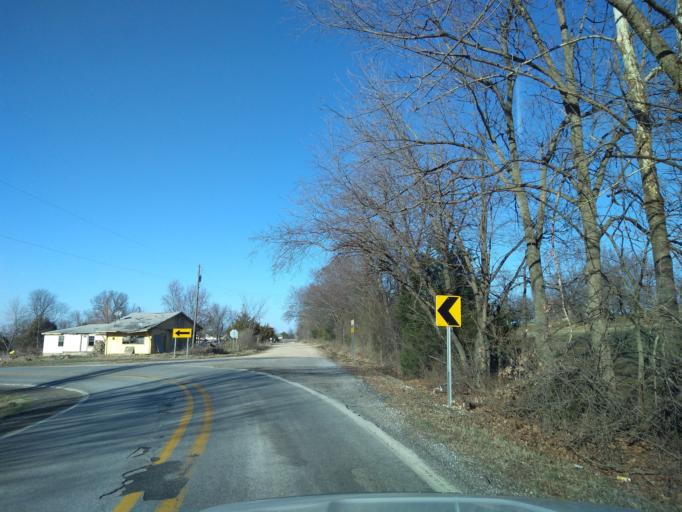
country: US
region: Arkansas
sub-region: Washington County
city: Lincoln
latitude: 35.9457
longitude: -94.3754
